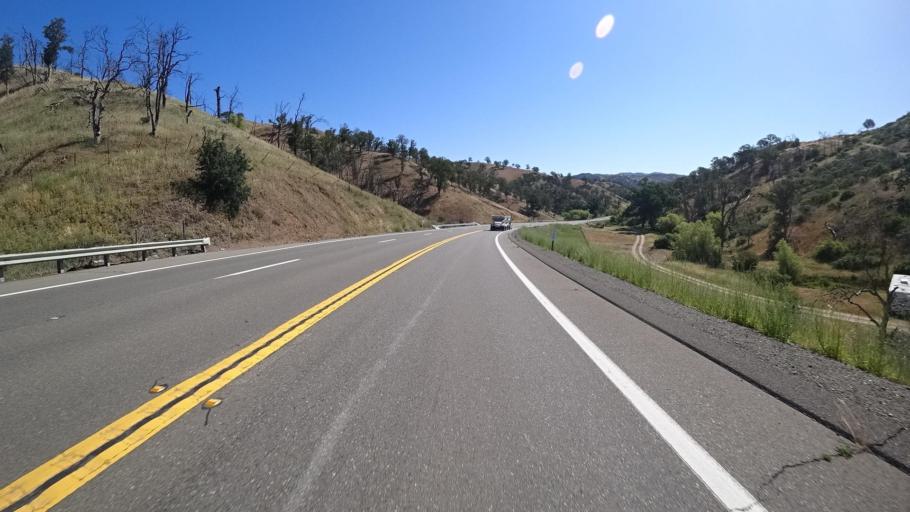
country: US
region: California
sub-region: Lake County
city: Clearlake
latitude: 39.0166
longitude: -122.5862
